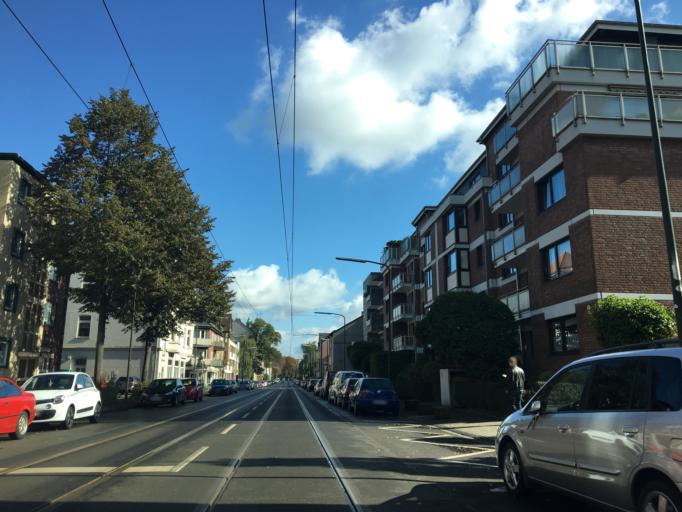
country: DE
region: North Rhine-Westphalia
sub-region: Regierungsbezirk Dusseldorf
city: Hilden
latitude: 51.1622
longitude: 6.8612
